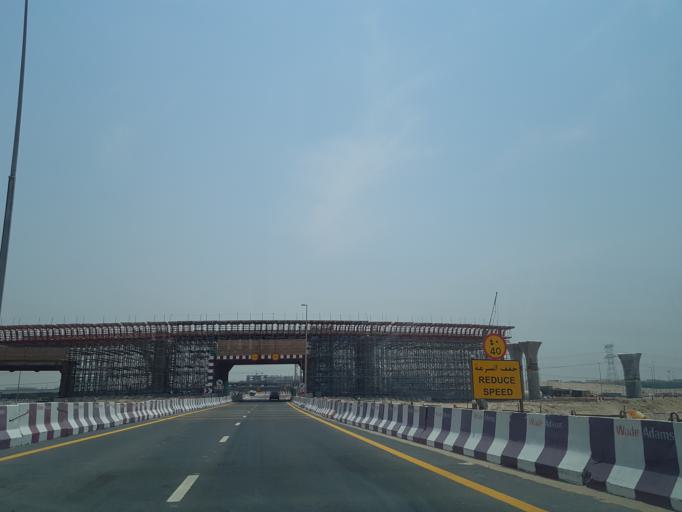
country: AE
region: Dubai
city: Dubai
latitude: 24.9987
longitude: 55.1887
